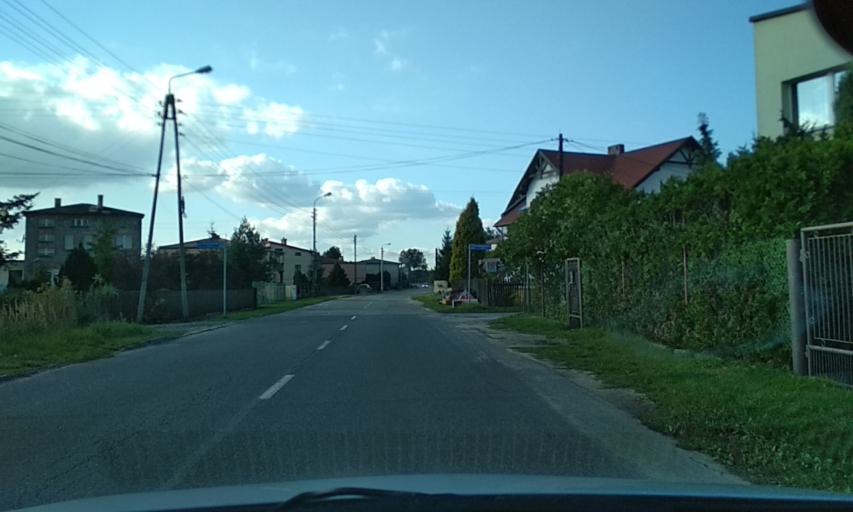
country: PL
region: Silesian Voivodeship
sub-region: Powiat bierunsko-ledzinski
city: Ledziny
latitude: 50.1721
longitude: 19.1455
